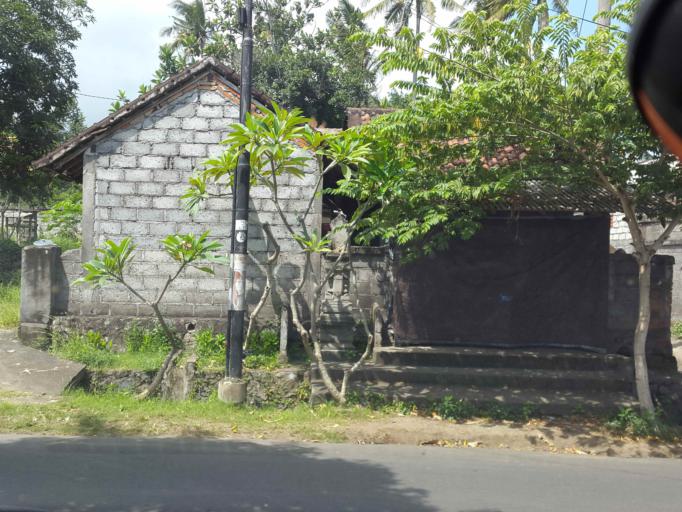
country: ID
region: Bali
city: Klungkung
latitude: -8.5381
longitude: 115.3829
